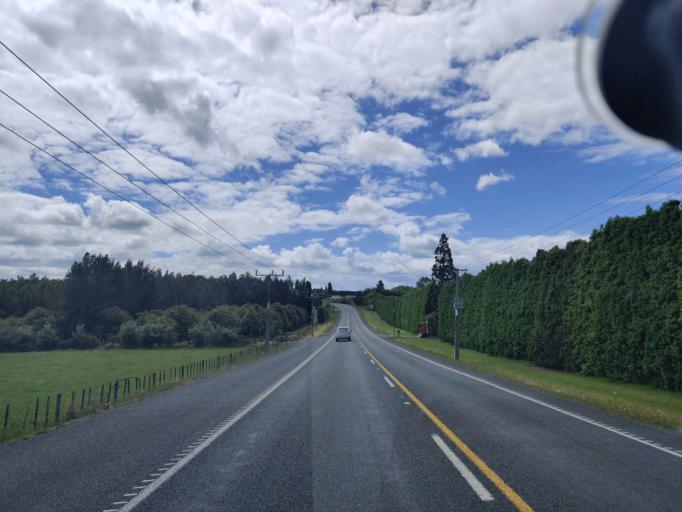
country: NZ
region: Northland
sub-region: Far North District
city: Kerikeri
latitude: -35.1799
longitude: 173.9074
